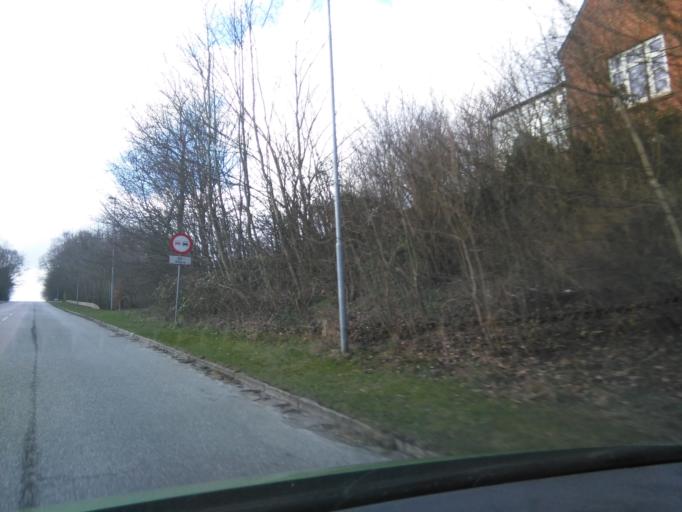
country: DK
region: Central Jutland
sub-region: Arhus Kommune
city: Malling
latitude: 56.0342
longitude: 10.1894
